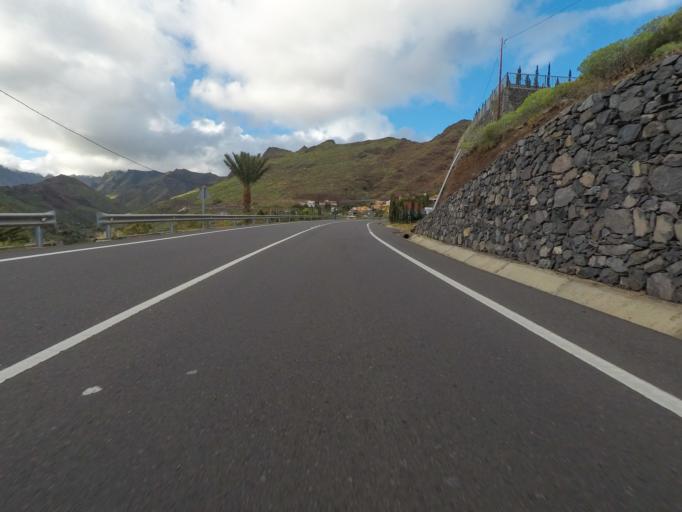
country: ES
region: Canary Islands
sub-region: Provincia de Santa Cruz de Tenerife
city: San Sebastian de la Gomera
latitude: 28.1063
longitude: -17.1250
